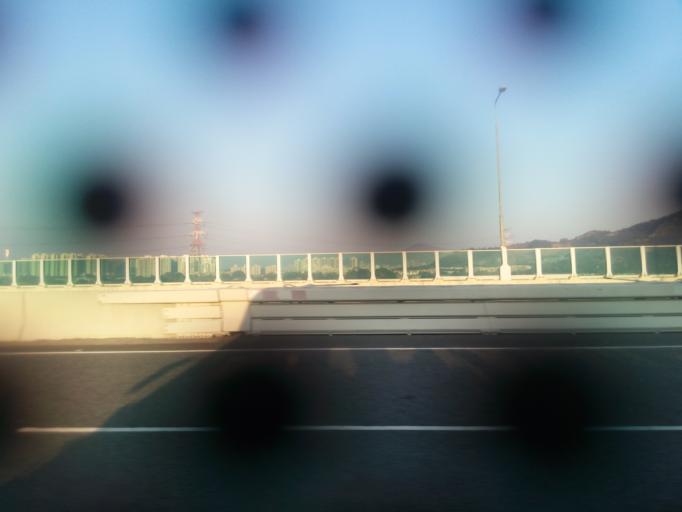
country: HK
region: Tuen Mun
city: Tuen Mun
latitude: 22.4242
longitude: 113.9838
